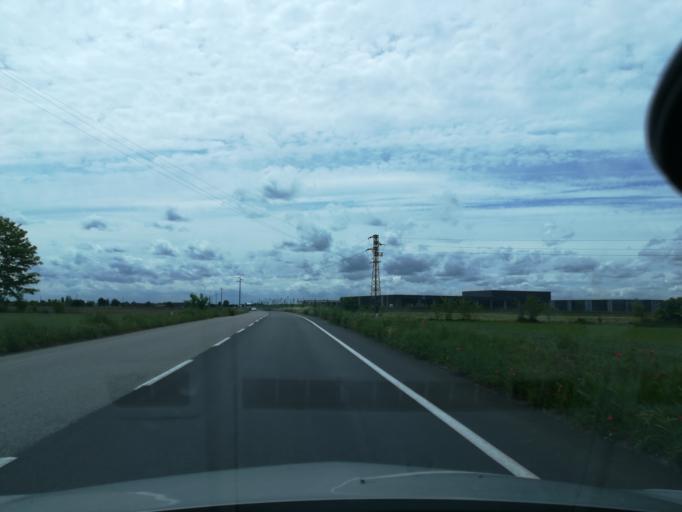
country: IT
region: Lombardy
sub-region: Provincia di Bergamo
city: Calcio
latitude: 45.5194
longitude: 9.8332
